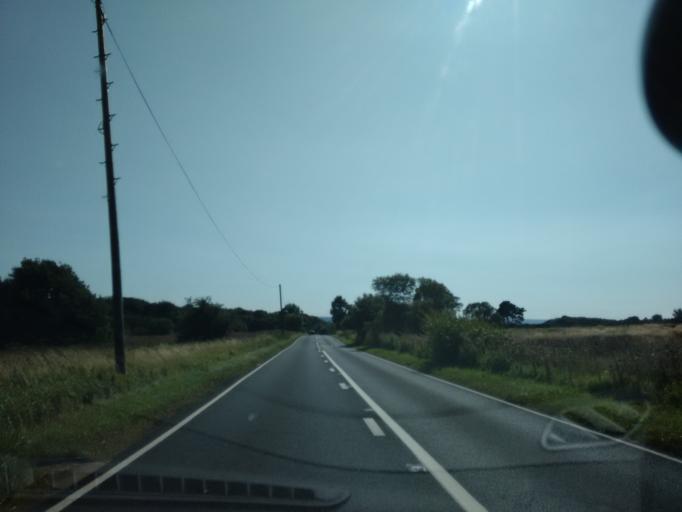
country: GB
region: England
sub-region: Northumberland
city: Corbridge
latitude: 55.0062
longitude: -2.0211
